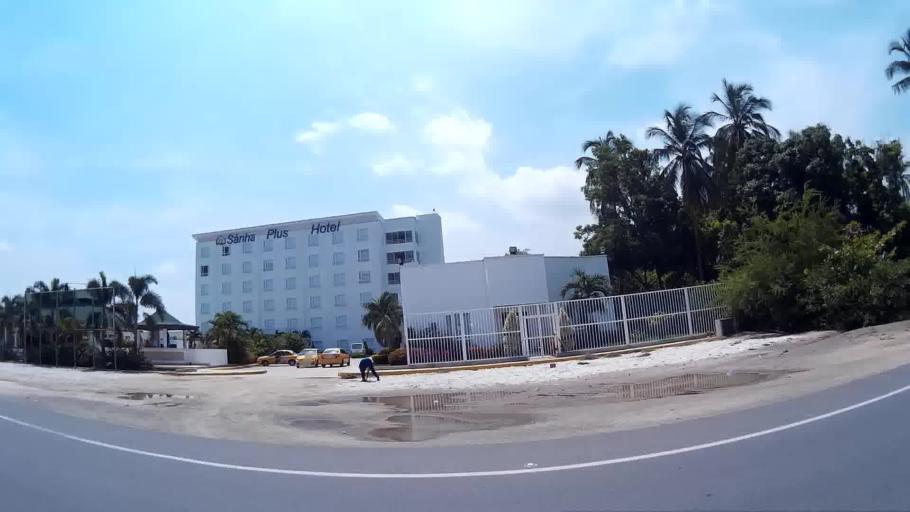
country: CO
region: Magdalena
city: Santa Marta
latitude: 11.1572
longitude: -74.2231
